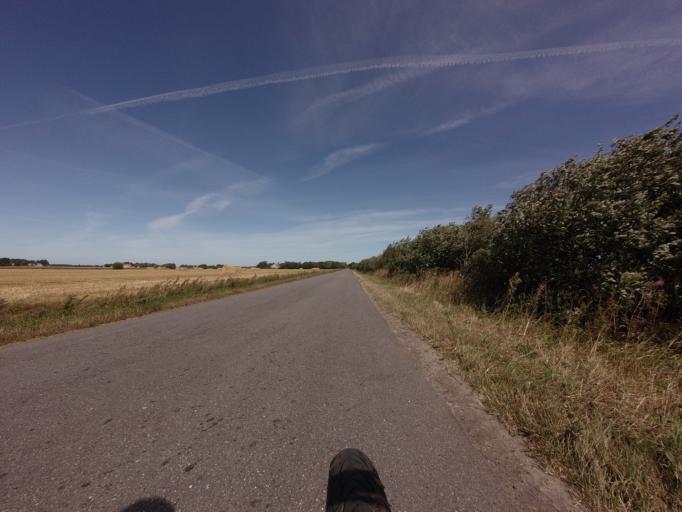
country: DK
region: North Denmark
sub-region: Bronderslev Kommune
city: Bronderslev
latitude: 57.3166
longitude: 9.8141
